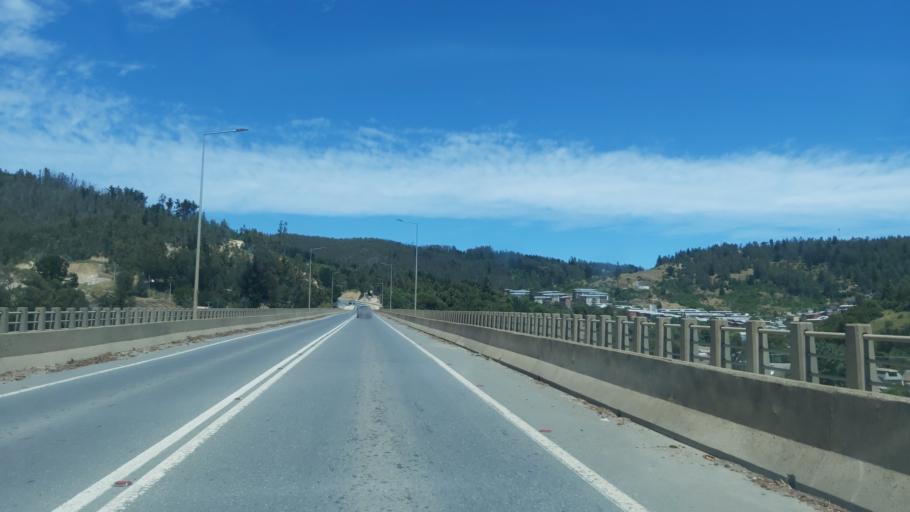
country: CL
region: Maule
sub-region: Provincia de Talca
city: Constitucion
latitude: -35.3411
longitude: -72.3930
